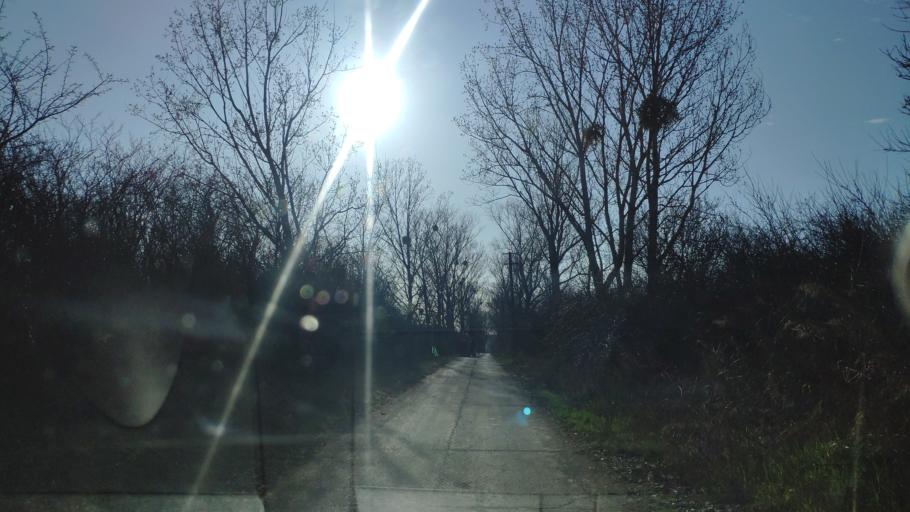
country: SK
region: Kosicky
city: Kosice
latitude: 48.6543
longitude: 21.2547
